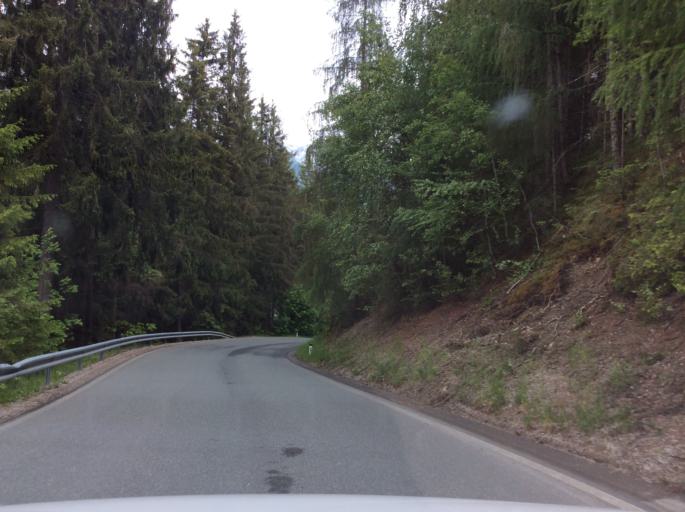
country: AT
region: Styria
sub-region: Politischer Bezirk Liezen
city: Schladming
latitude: 47.3939
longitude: 13.7107
